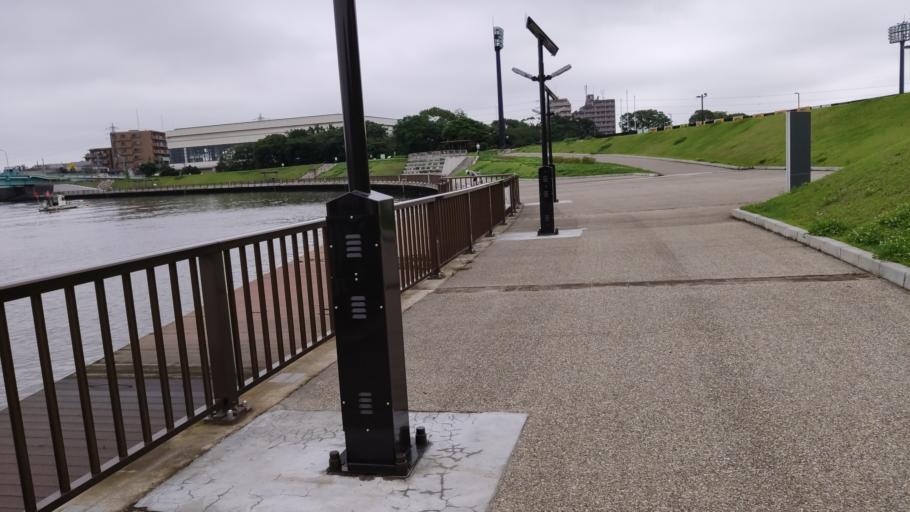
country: JP
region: Chiba
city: Matsudo
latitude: 35.7363
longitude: 139.8600
